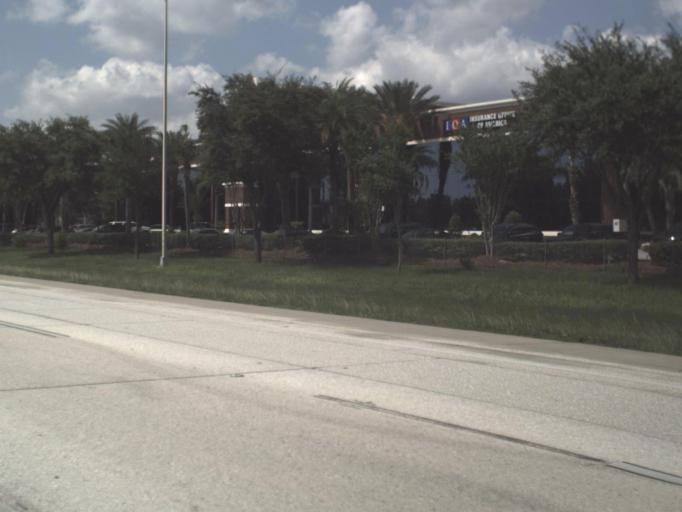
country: US
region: Florida
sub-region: Duval County
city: Jacksonville
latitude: 30.2518
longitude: -81.5967
